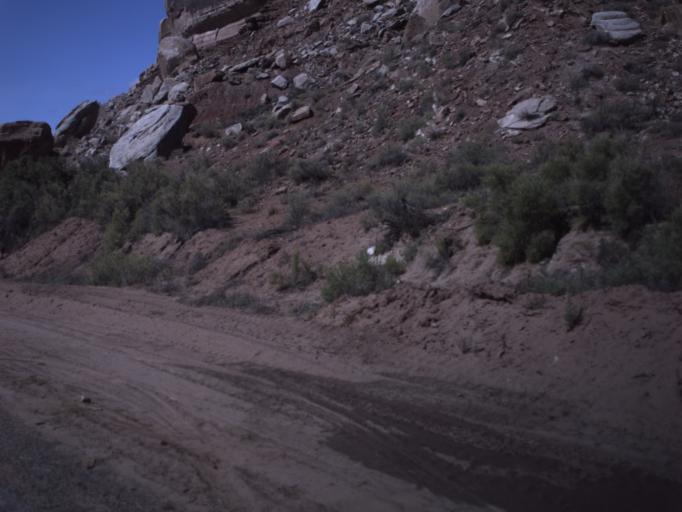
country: US
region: Utah
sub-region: San Juan County
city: Blanding
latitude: 37.2851
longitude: -109.5254
